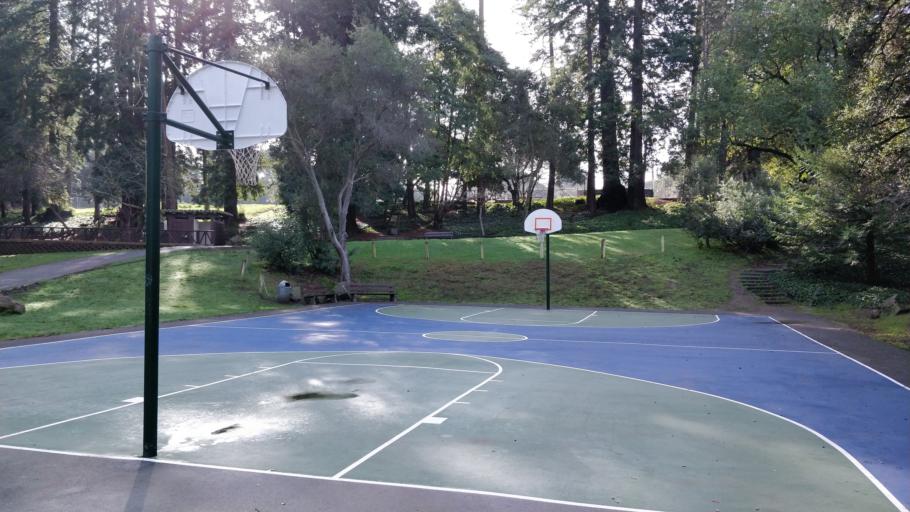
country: US
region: California
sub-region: Alameda County
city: Berkeley
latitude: 37.8859
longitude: -122.2622
